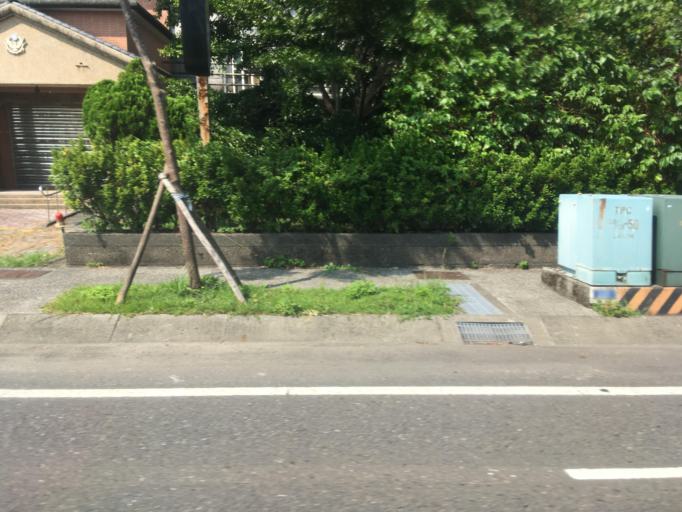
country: TW
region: Taiwan
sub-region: Yilan
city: Yilan
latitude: 24.6121
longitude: 121.8525
